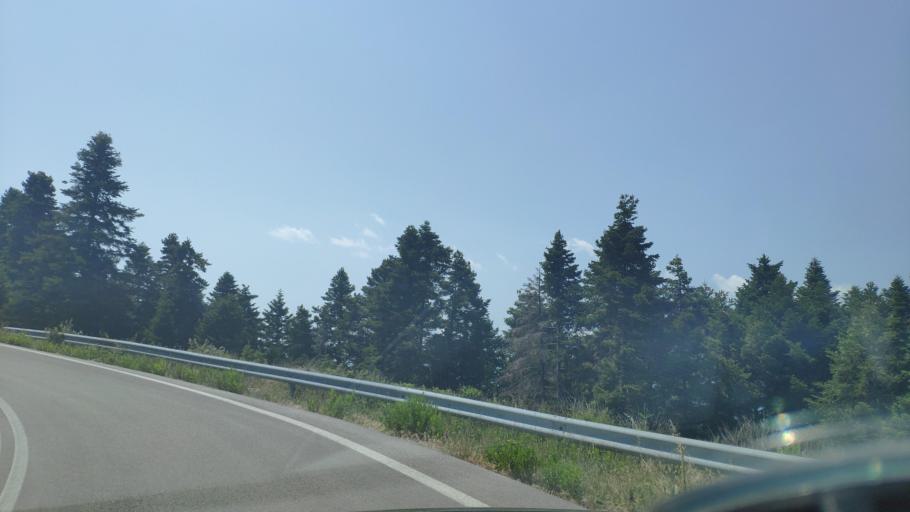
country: GR
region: Epirus
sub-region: Nomos Artas
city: Ano Kalentini
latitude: 39.2726
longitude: 21.2752
